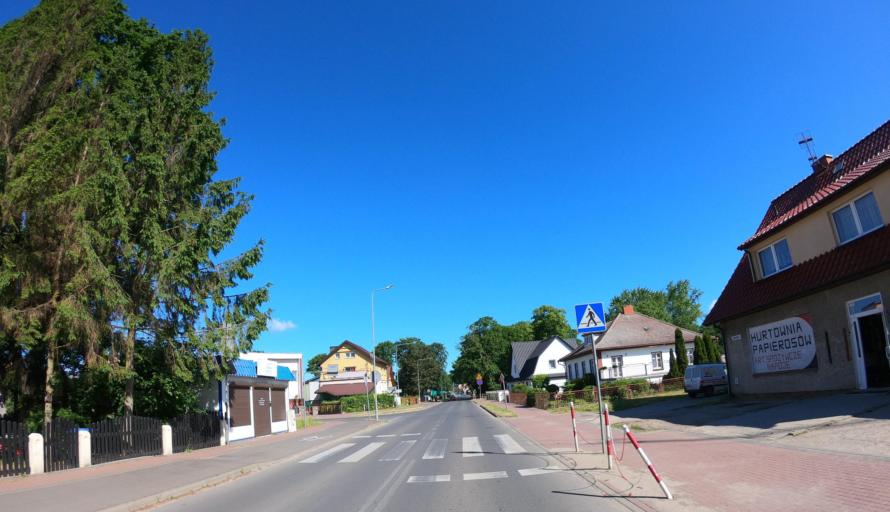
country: PL
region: West Pomeranian Voivodeship
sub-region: Powiat kamienski
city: Kamien Pomorski
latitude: 53.9625
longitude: 14.7744
